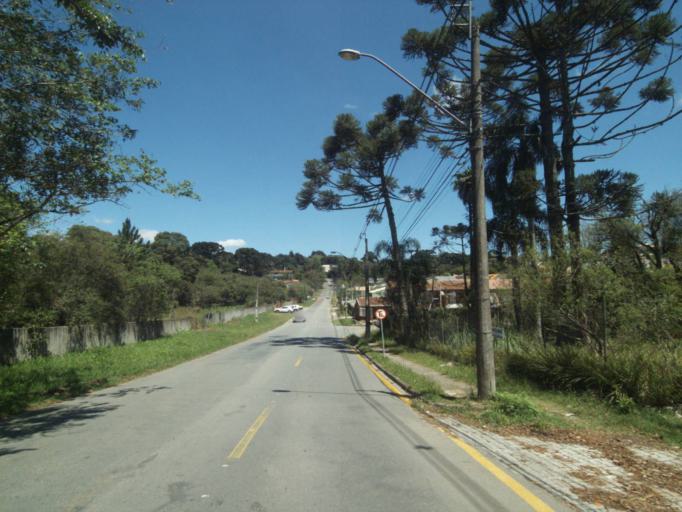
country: BR
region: Parana
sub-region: Curitiba
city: Curitiba
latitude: -25.3788
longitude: -49.2663
